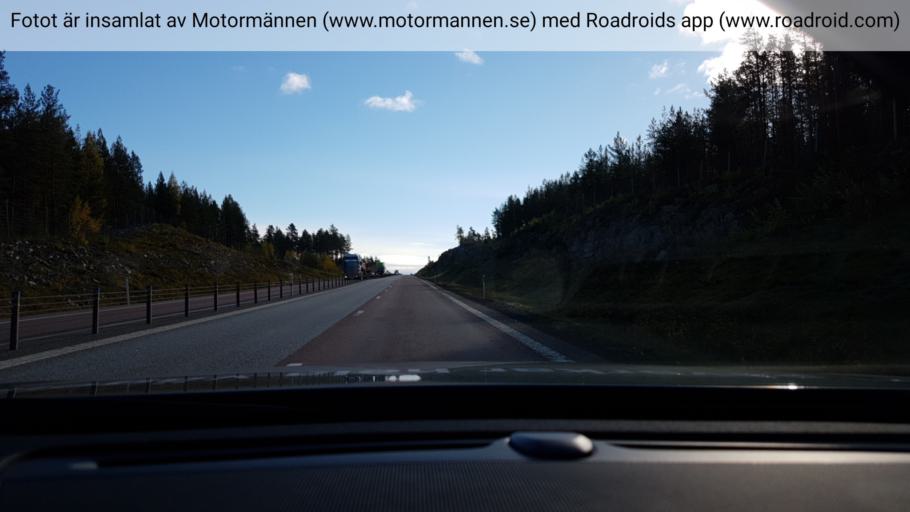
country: SE
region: Vaesterbotten
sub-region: Skelleftea Kommun
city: Soedra Bergsbyn
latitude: 64.6914
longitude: 21.0357
